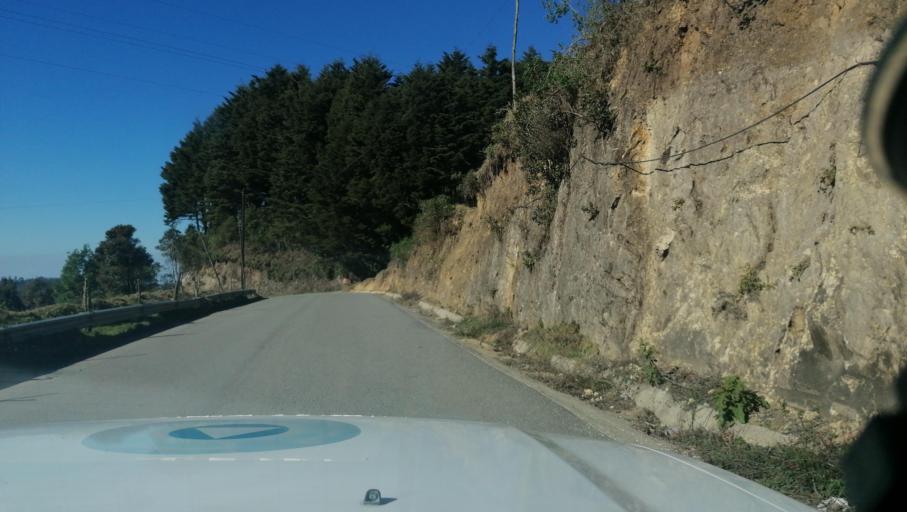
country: MX
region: Chiapas
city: Motozintla de Mendoza
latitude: 15.2701
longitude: -92.2289
